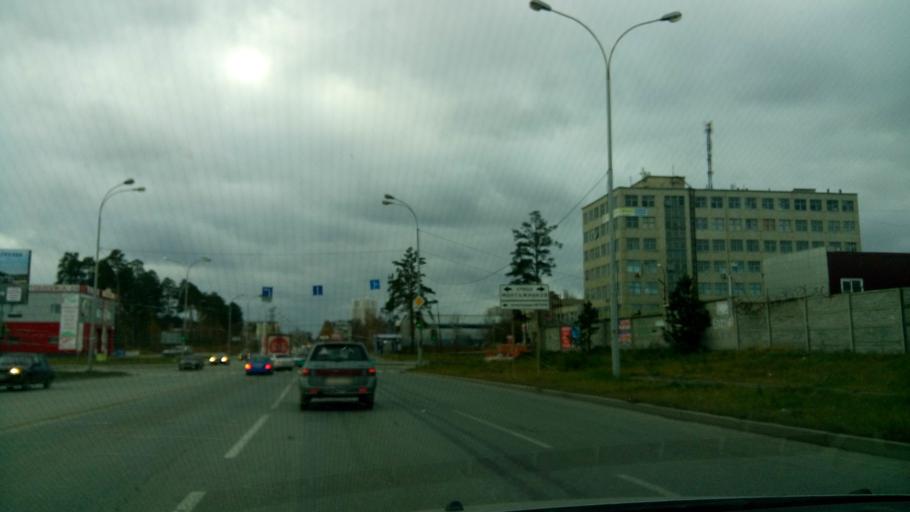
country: RU
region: Sverdlovsk
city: Shuvakish
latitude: 56.8880
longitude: 60.5275
